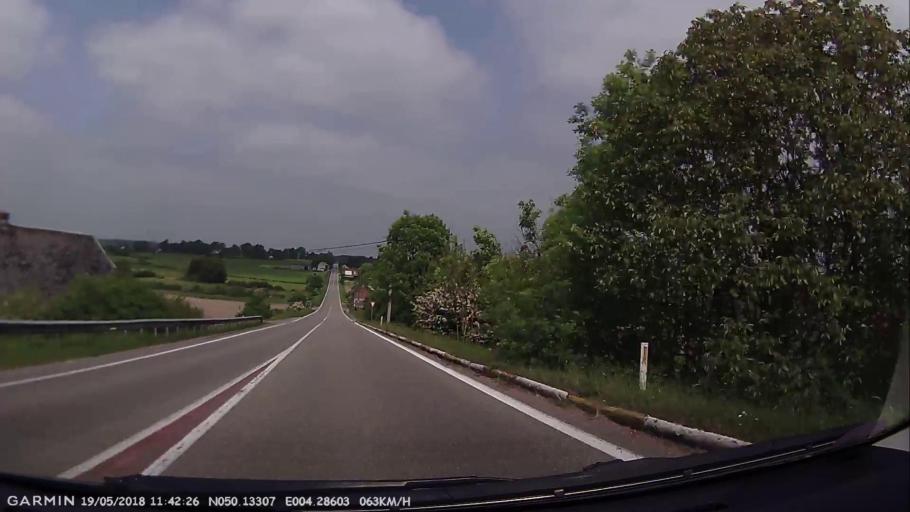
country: BE
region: Wallonia
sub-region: Province du Hainaut
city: Froidchapelle
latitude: 50.1332
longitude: 4.2859
